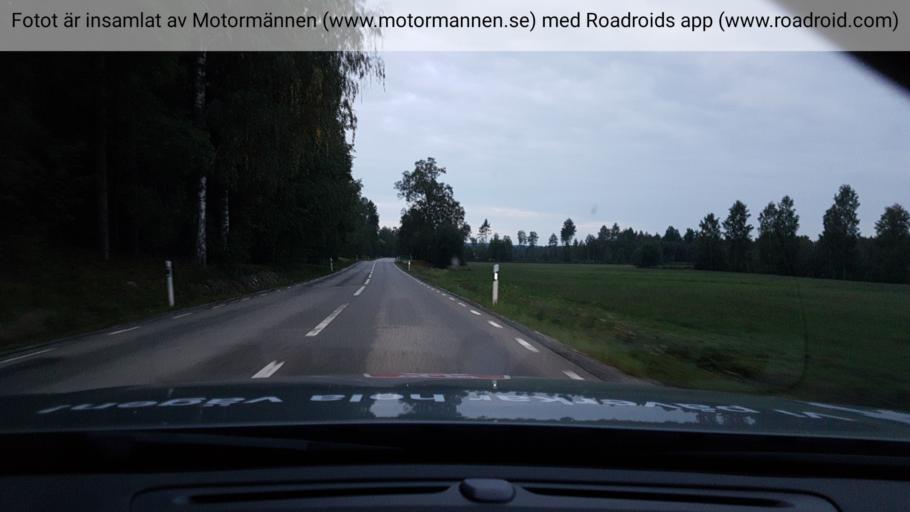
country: SE
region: OErebro
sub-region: Nora Kommun
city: As
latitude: 59.4691
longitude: 14.9048
